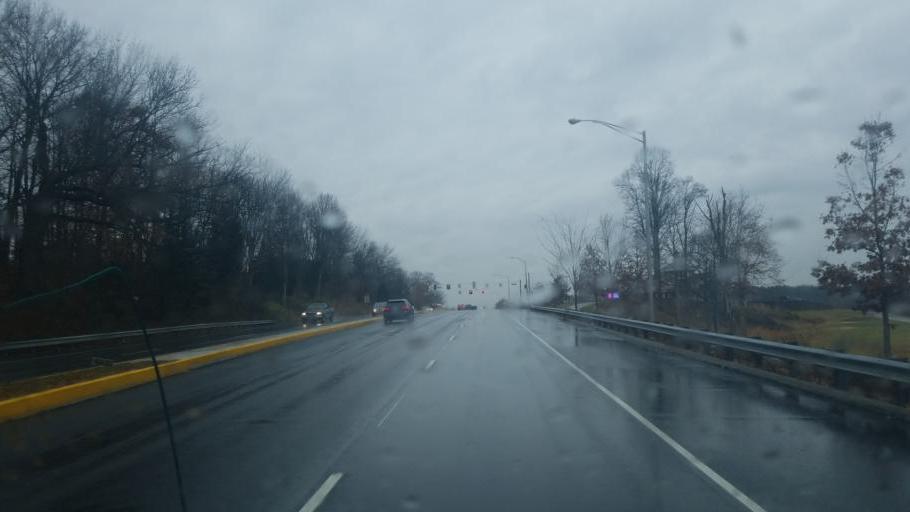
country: US
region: Indiana
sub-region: Bartholomew County
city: Columbus
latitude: 39.2000
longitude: -85.9662
